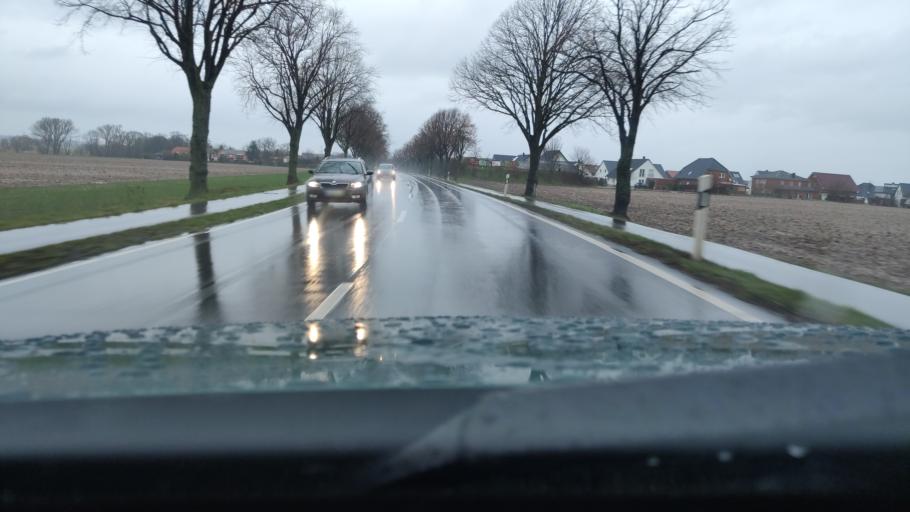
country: DE
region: Lower Saxony
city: Ilsede
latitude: 52.2789
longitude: 10.2272
